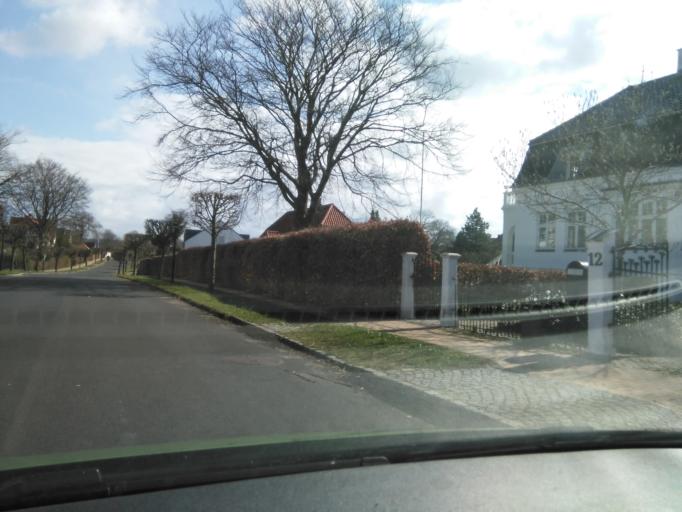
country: DK
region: South Denmark
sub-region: Middelfart Kommune
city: Strib
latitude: 55.5429
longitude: 9.7641
